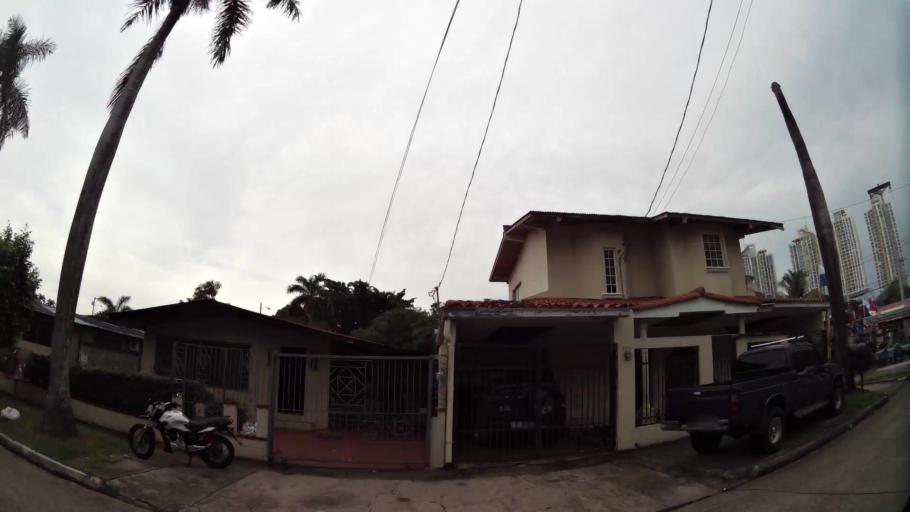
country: PA
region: Panama
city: Panama
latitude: 9.0242
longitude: -79.5207
